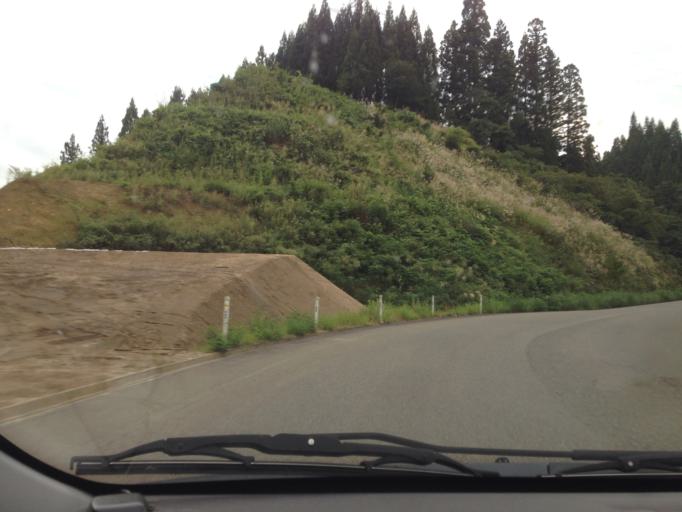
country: JP
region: Fukushima
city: Kitakata
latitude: 37.4667
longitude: 139.6476
